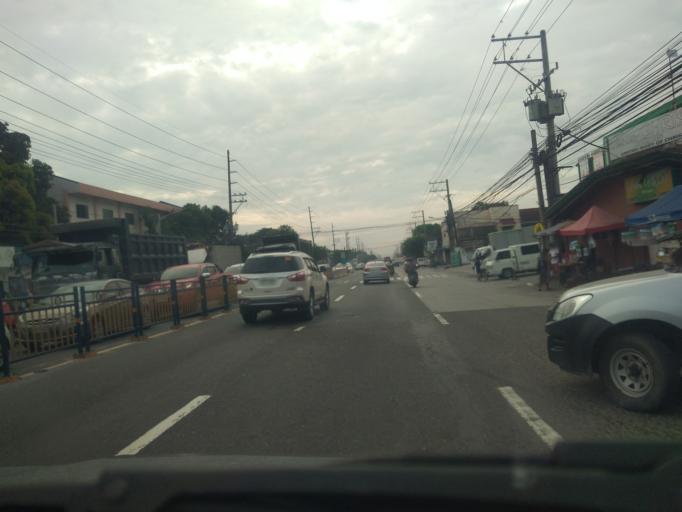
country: PH
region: Central Luzon
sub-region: Province of Pampanga
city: Bulaon
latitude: 15.0766
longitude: 120.6416
